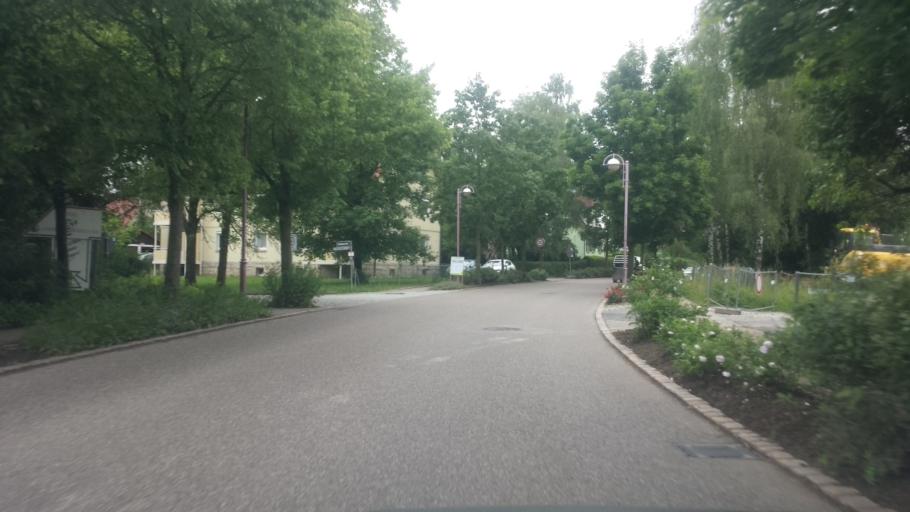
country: DE
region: Baden-Wuerttemberg
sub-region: Regierungsbezirk Stuttgart
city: Rot am See
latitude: 49.2537
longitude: 10.0235
